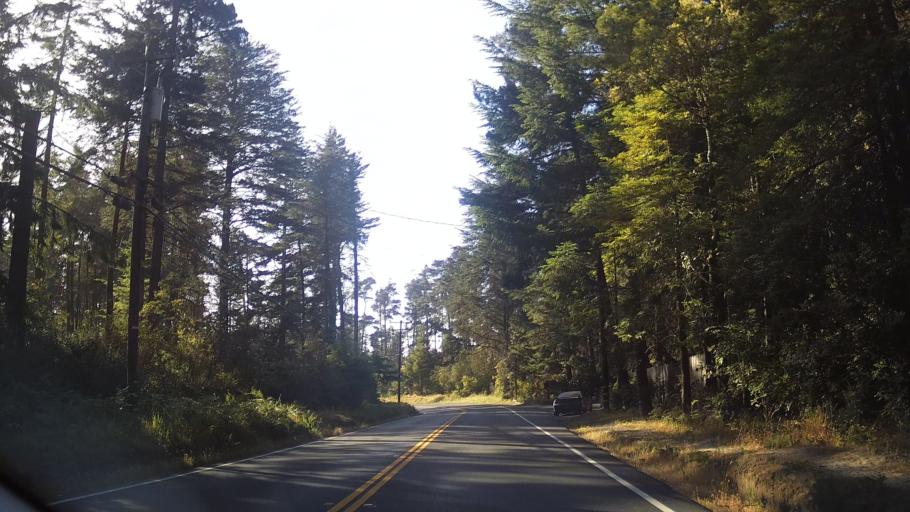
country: US
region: California
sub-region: Mendocino County
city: Fort Bragg
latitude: 39.4101
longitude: -123.7468
